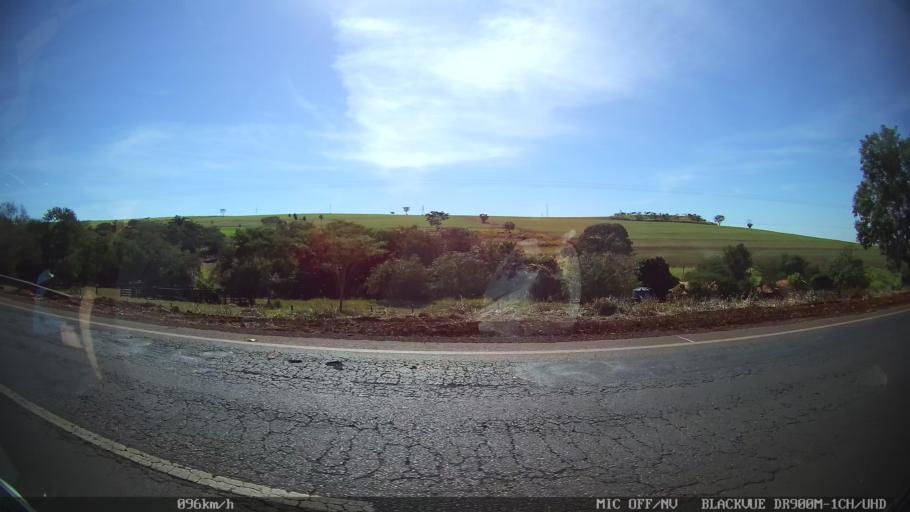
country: BR
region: Sao Paulo
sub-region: Ipua
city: Ipua
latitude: -20.4928
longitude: -48.0139
